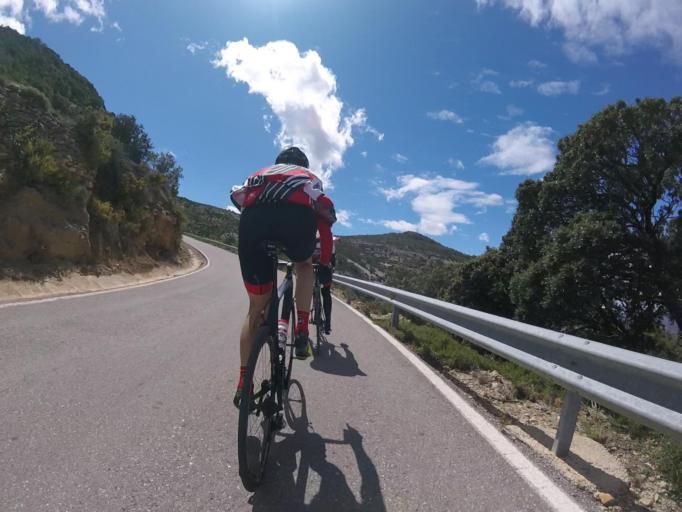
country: ES
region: Valencia
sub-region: Provincia de Castello
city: Sierra-Engarceran
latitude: 40.2852
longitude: -0.0361
